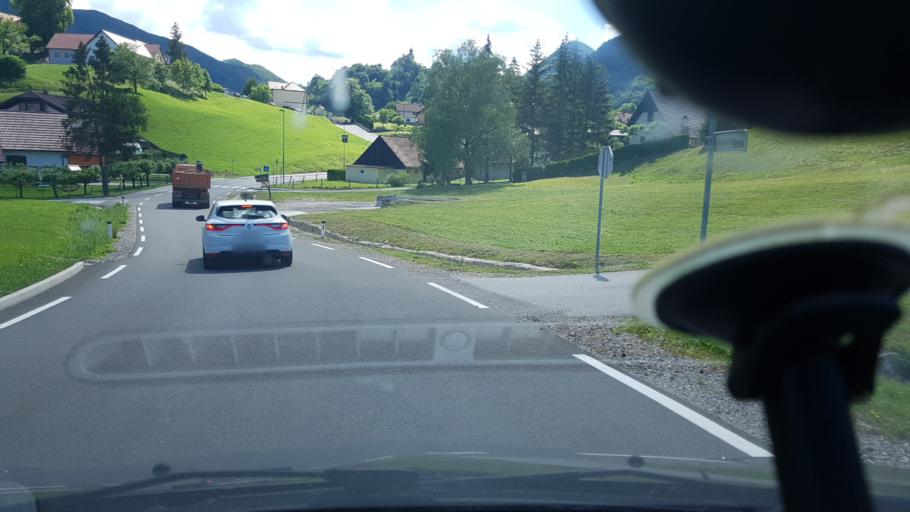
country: SI
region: Zetale
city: Zetale
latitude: 46.2759
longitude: 15.7942
